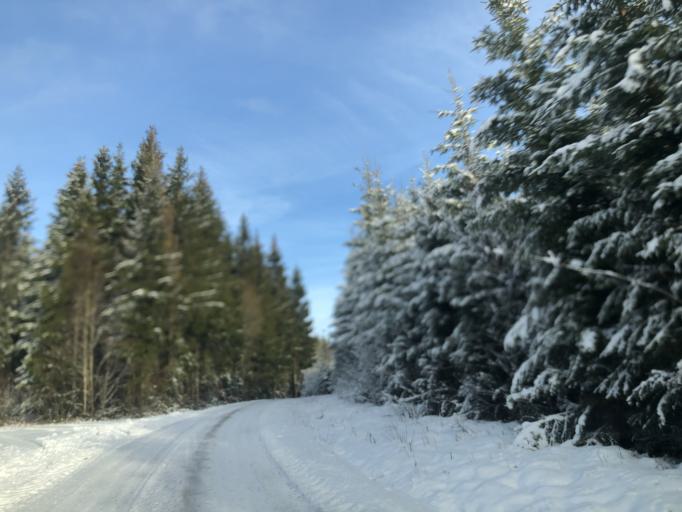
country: SE
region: Vaestra Goetaland
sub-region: Ulricehamns Kommun
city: Ulricehamn
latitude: 57.7395
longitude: 13.4942
